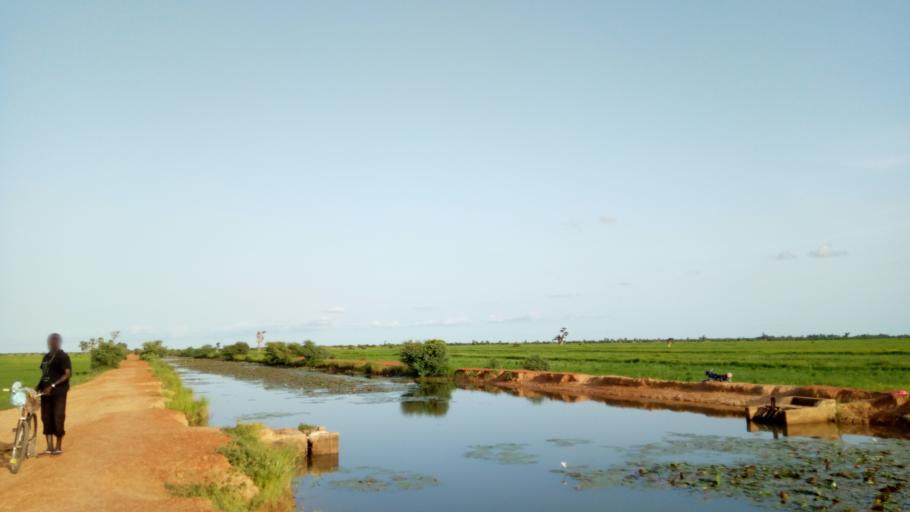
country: ML
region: Segou
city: Niono
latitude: 14.3027
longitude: -5.9317
